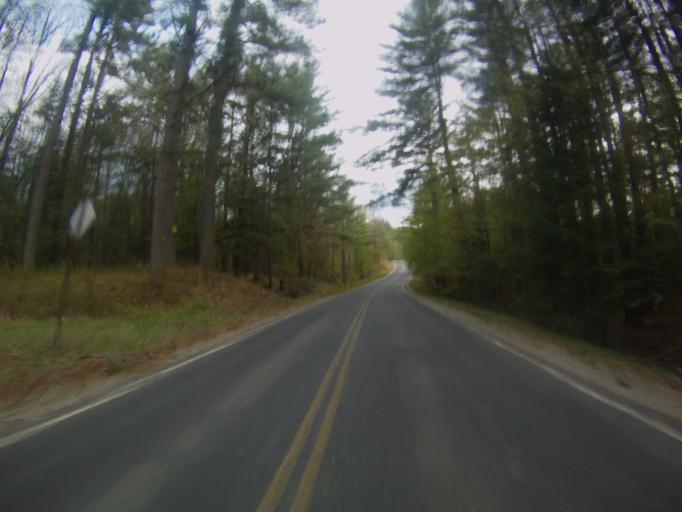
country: US
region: New York
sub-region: Warren County
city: Warrensburg
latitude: 43.8163
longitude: -73.9345
